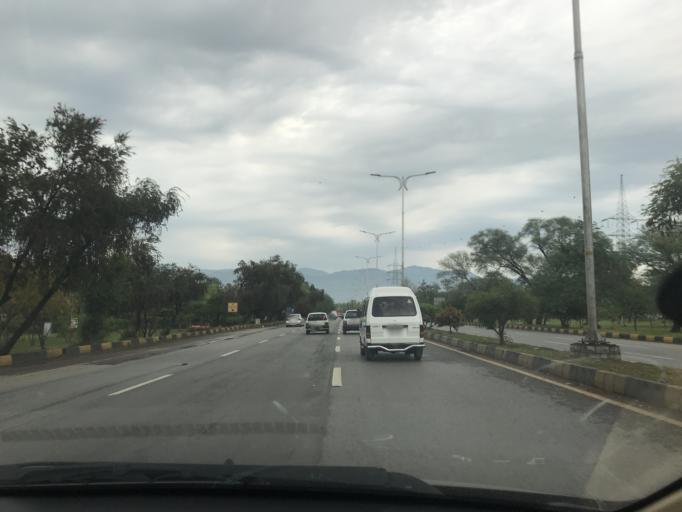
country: PK
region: Islamabad
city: Islamabad
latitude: 33.6938
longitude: 73.1102
